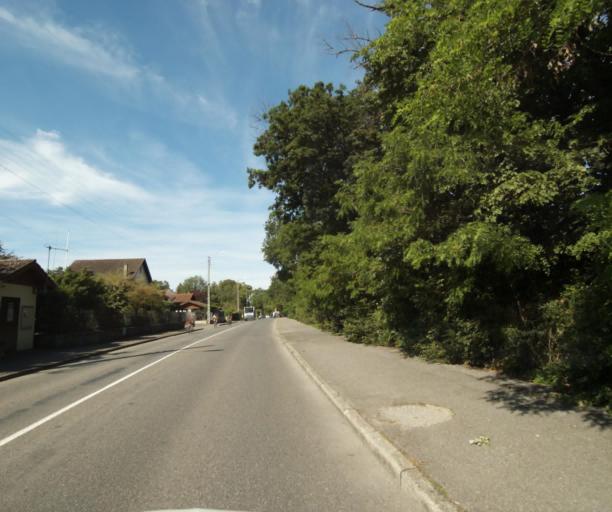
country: FR
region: Rhone-Alpes
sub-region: Departement de la Haute-Savoie
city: Thonon-les-Bains
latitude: 46.3673
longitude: 6.4590
